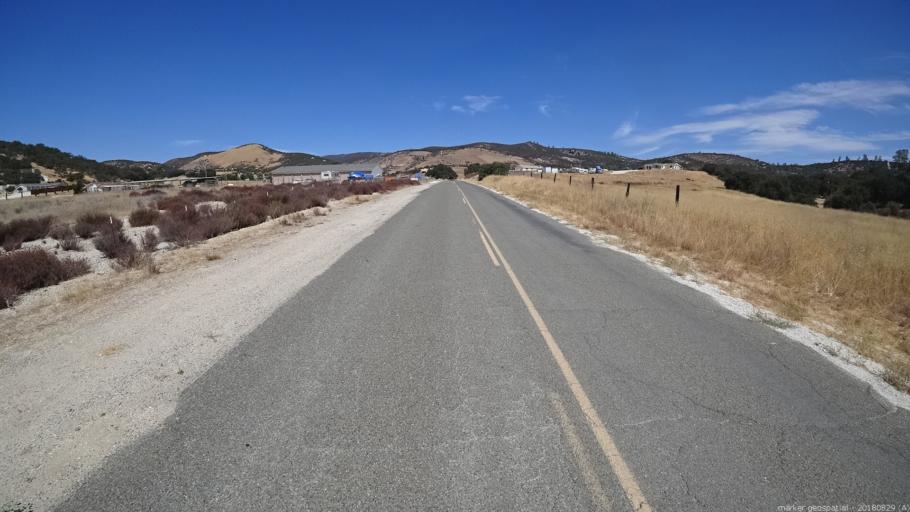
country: US
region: California
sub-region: San Luis Obispo County
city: Lake Nacimiento
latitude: 35.9013
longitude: -120.9841
